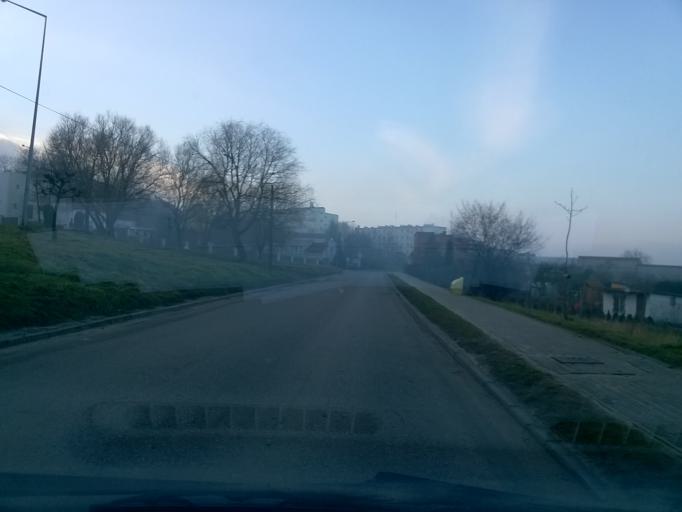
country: PL
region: Kujawsko-Pomorskie
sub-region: Powiat nakielski
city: Kcynia
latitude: 52.9947
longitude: 17.4874
